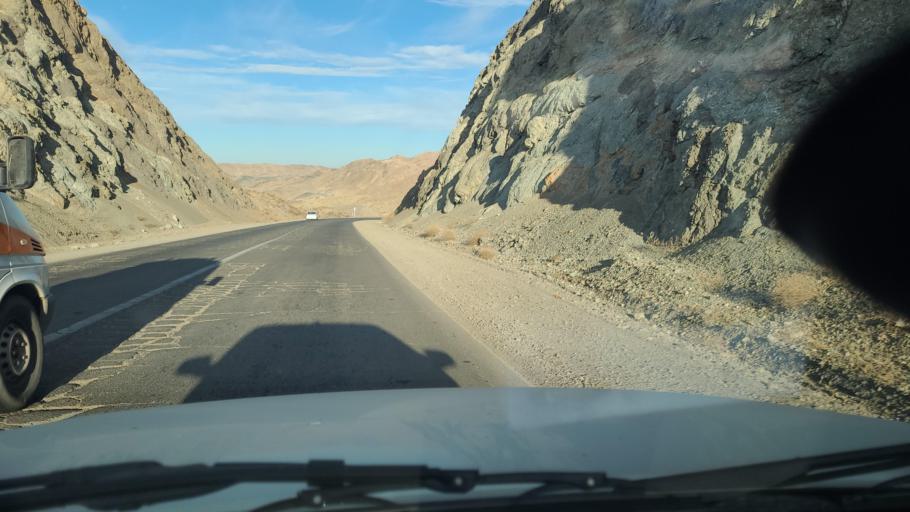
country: IR
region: Razavi Khorasan
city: Sabzevar
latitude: 36.4181
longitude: 57.5552
